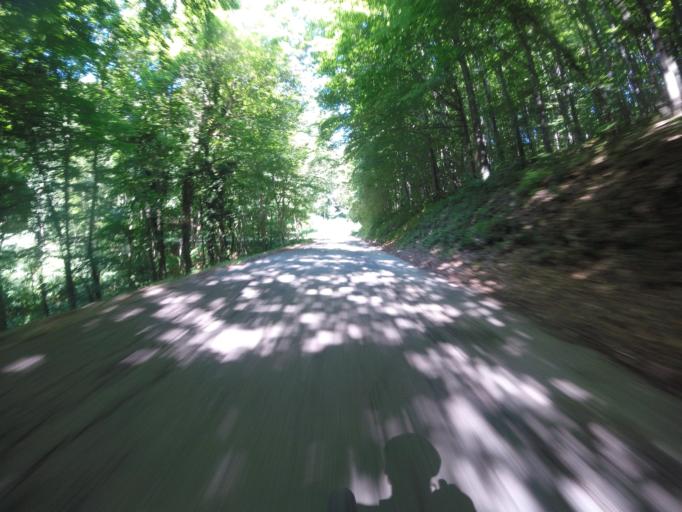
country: SI
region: Kostanjevica na Krki
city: Kostanjevica na Krki
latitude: 45.8199
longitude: 15.5207
